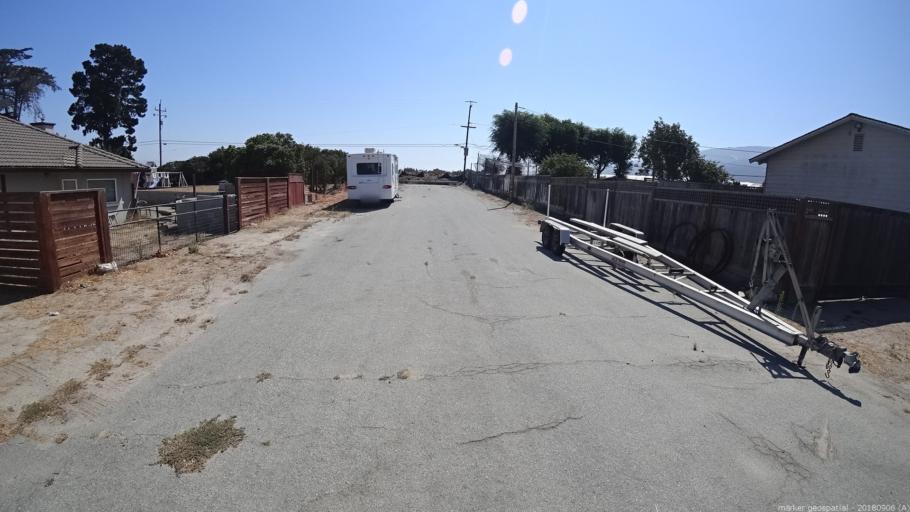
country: US
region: California
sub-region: Monterey County
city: Salinas
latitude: 36.5968
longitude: -121.6310
